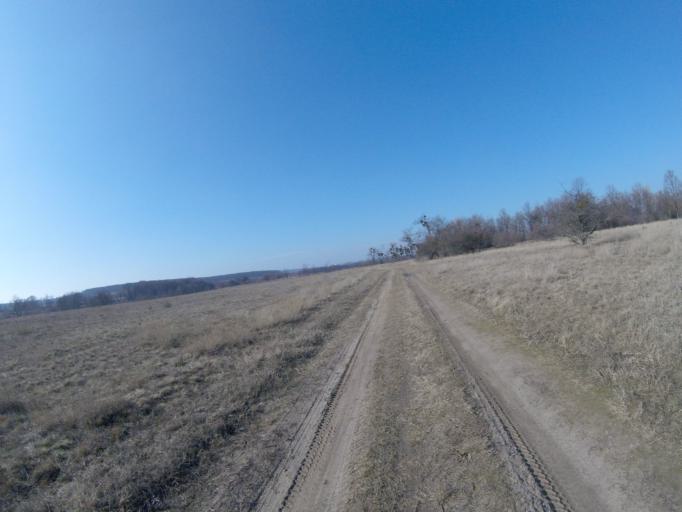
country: HU
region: Komarom-Esztergom
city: Oroszlany
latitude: 47.4623
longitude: 18.3485
